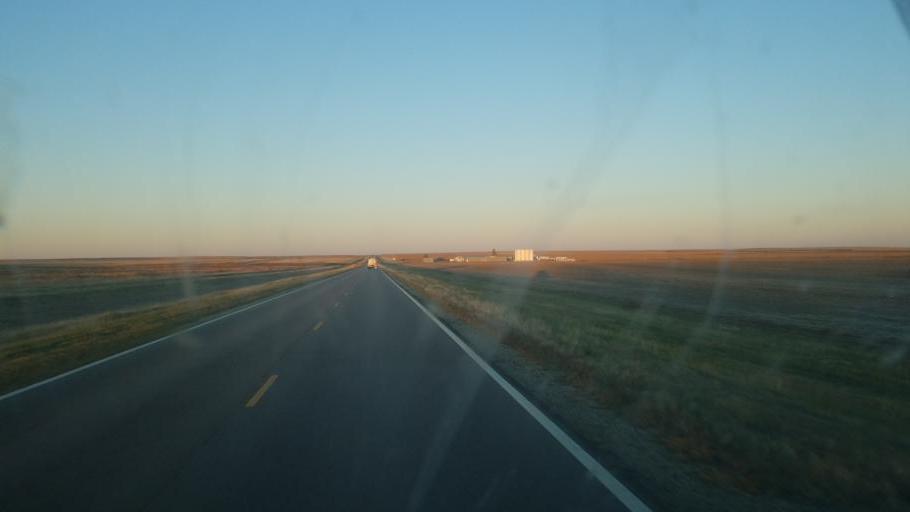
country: US
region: Kansas
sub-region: Wallace County
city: Sharon Springs
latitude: 38.9015
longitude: -101.7706
